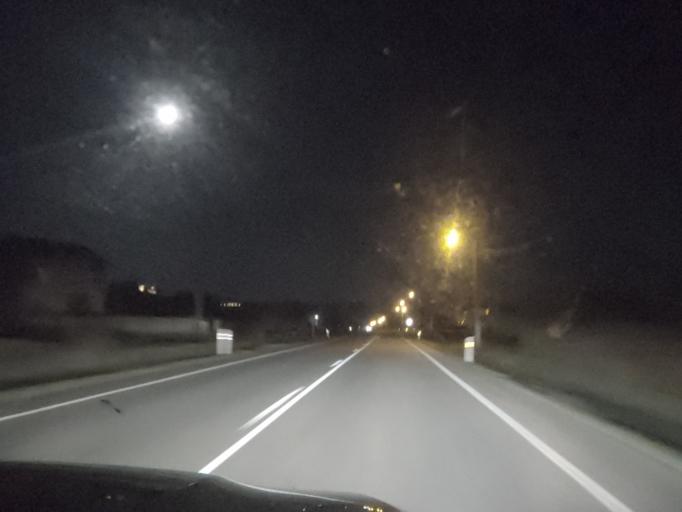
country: ES
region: Galicia
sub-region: Provincia de Ourense
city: Verin
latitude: 41.9456
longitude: -7.4824
